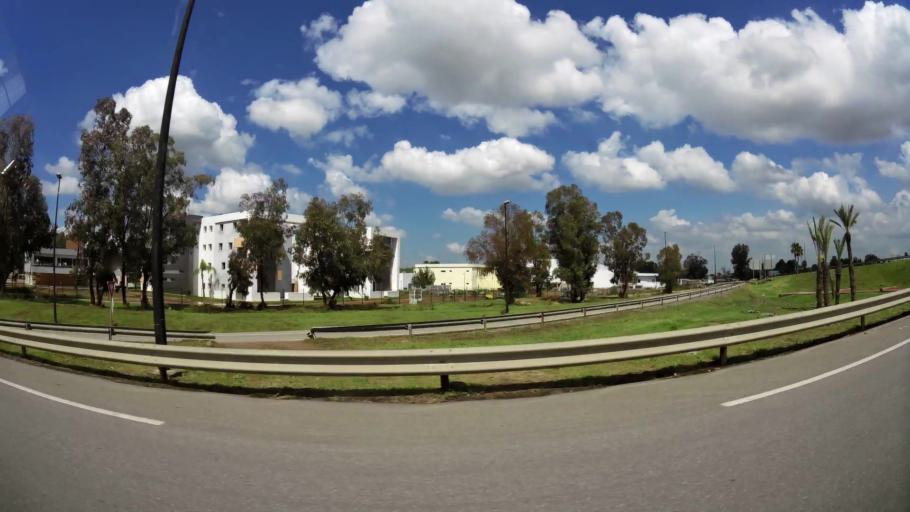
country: MA
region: Chaouia-Ouardigha
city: Nouaseur
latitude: 33.3794
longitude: -7.5706
